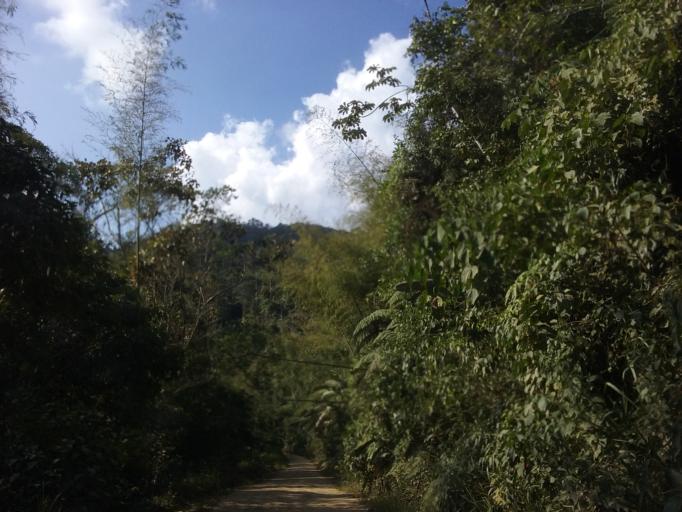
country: CO
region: Tolima
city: Libano
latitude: 4.8950
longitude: -75.0270
